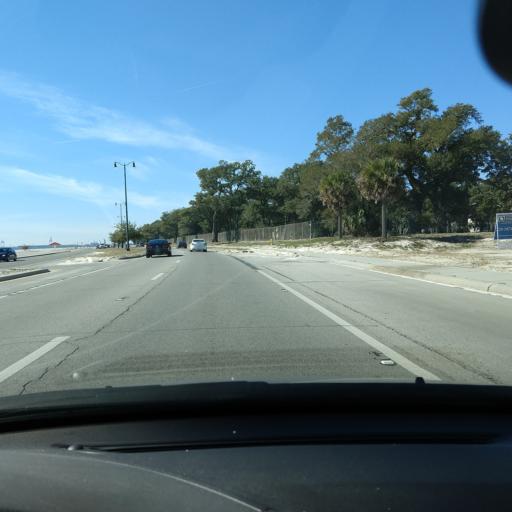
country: US
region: Mississippi
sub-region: Harrison County
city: Gulfport
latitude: 30.3775
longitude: -89.0491
